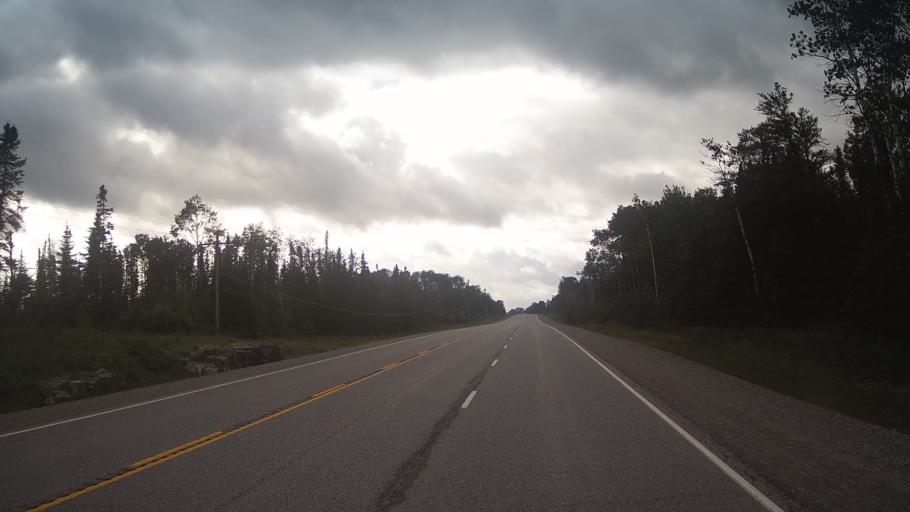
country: CA
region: Ontario
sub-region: Rainy River District
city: Atikokan
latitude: 49.0005
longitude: -90.4029
